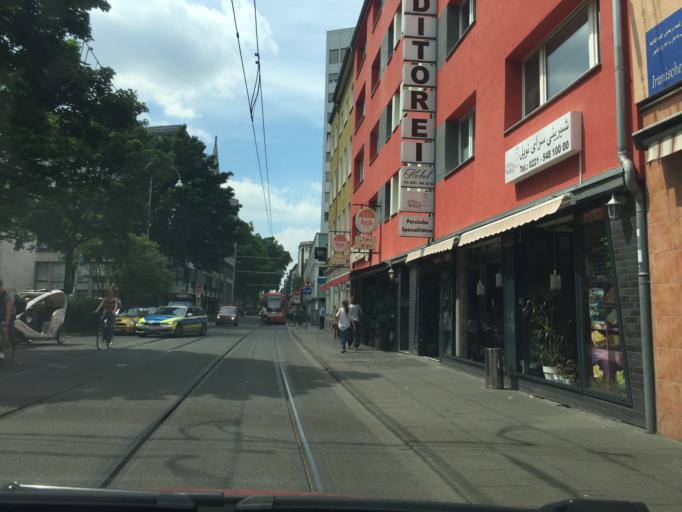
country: DE
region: North Rhine-Westphalia
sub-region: Regierungsbezirk Koln
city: Koeln
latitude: 50.9320
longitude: 6.9424
